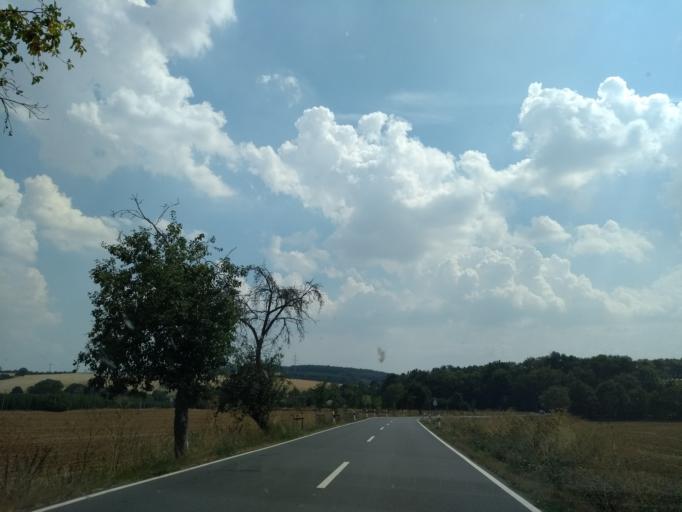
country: DE
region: Saxony-Anhalt
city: Kretzschau
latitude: 51.0251
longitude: 12.0764
